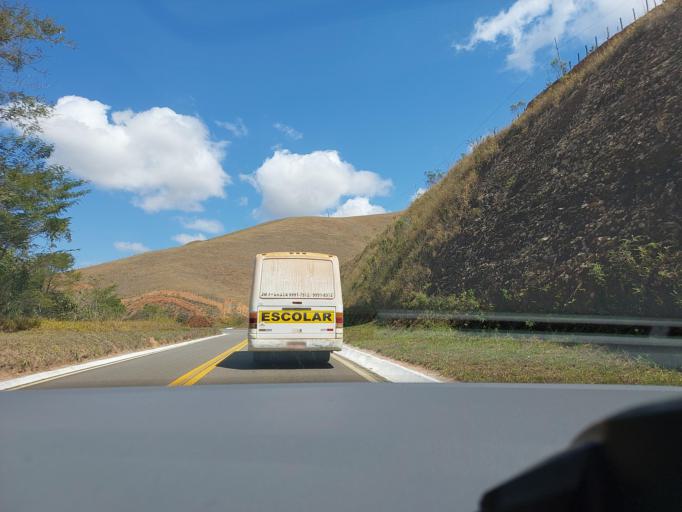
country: BR
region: Minas Gerais
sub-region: Muriae
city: Muriae
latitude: -21.0602
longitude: -42.5020
